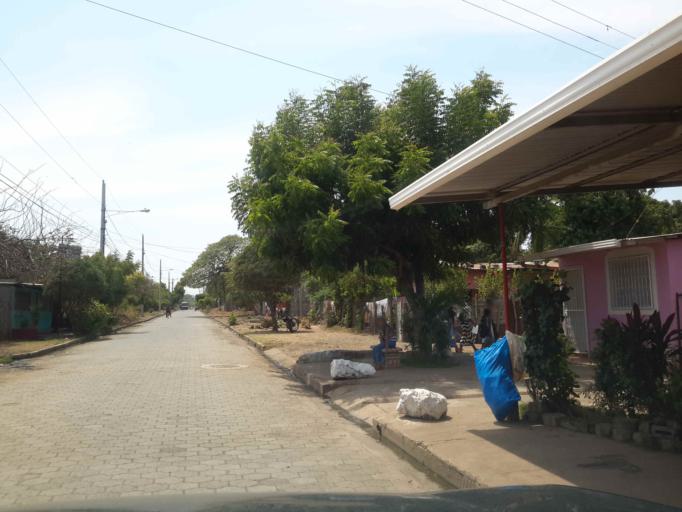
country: NI
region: Granada
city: Granada
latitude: 11.9443
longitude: -85.9591
